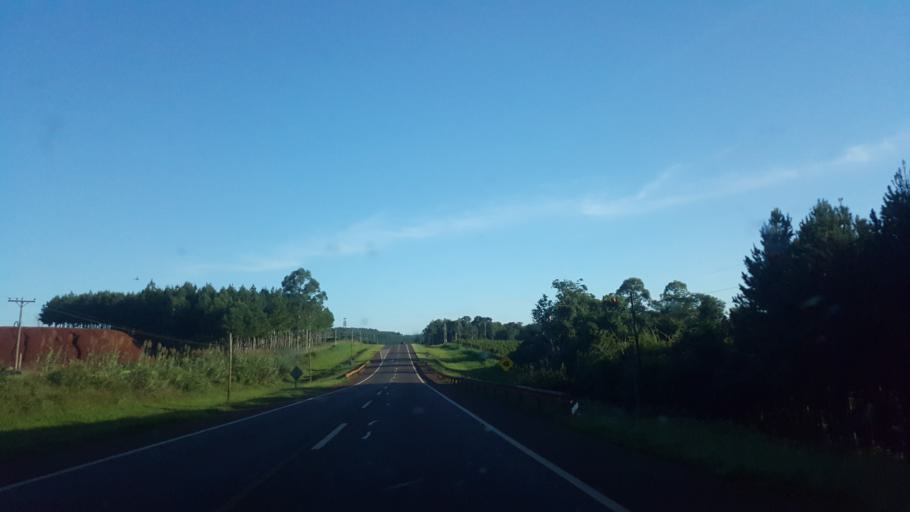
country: AR
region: Misiones
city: Caraguatay
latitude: -26.6479
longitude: -54.7543
